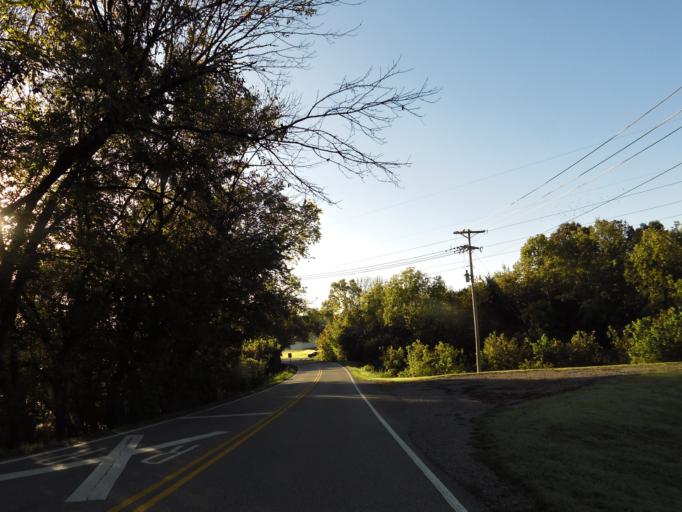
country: US
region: Tennessee
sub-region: Blount County
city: Eagleton Village
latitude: 35.8310
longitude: -83.9527
